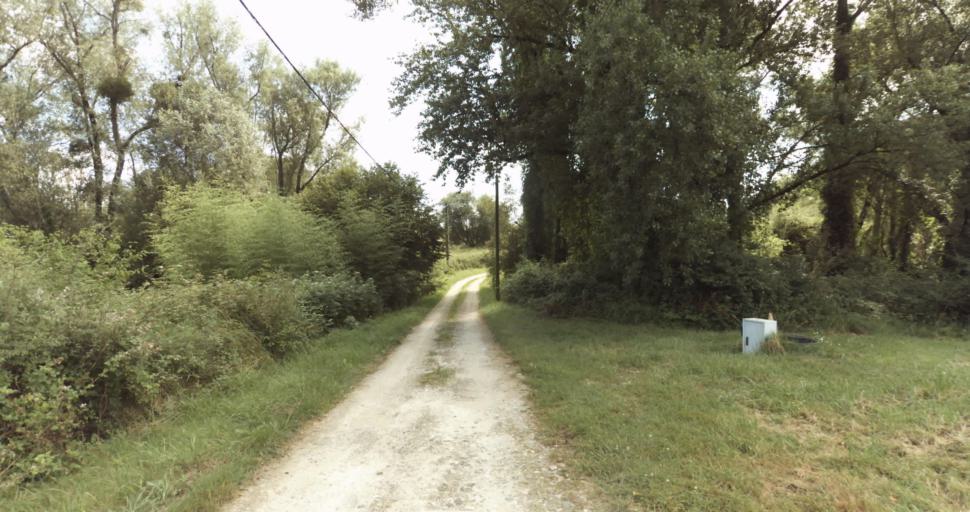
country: FR
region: Aquitaine
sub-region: Departement de la Gironde
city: Bazas
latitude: 44.4418
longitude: -0.2184
